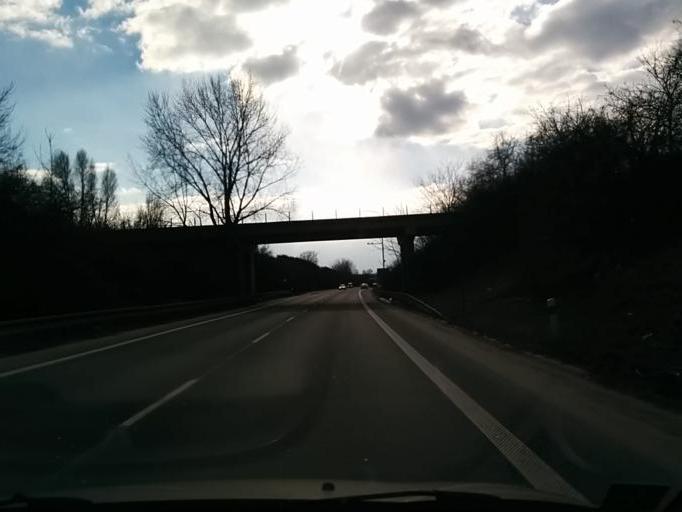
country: SK
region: Trnavsky
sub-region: Okres Trnava
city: Trnava
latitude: 48.3616
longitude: 17.6129
